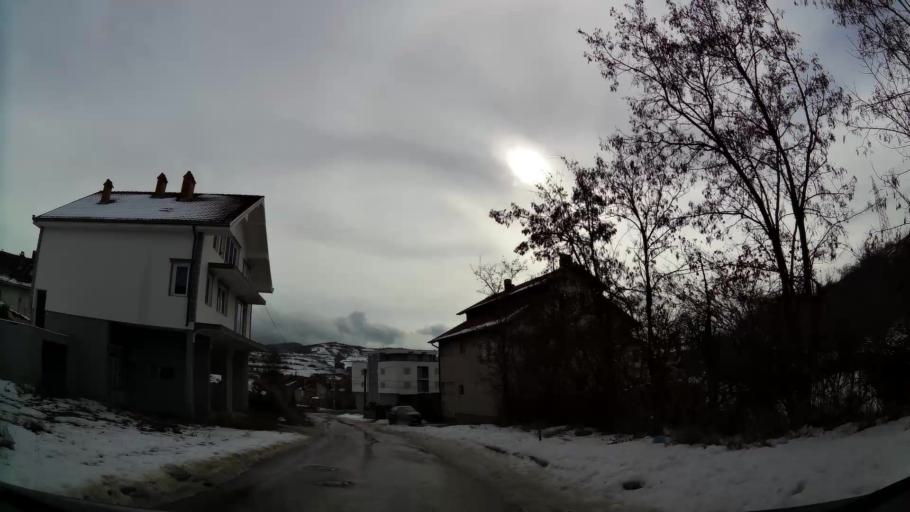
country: XK
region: Pristina
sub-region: Komuna e Prishtines
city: Pristina
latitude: 42.6898
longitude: 21.1778
